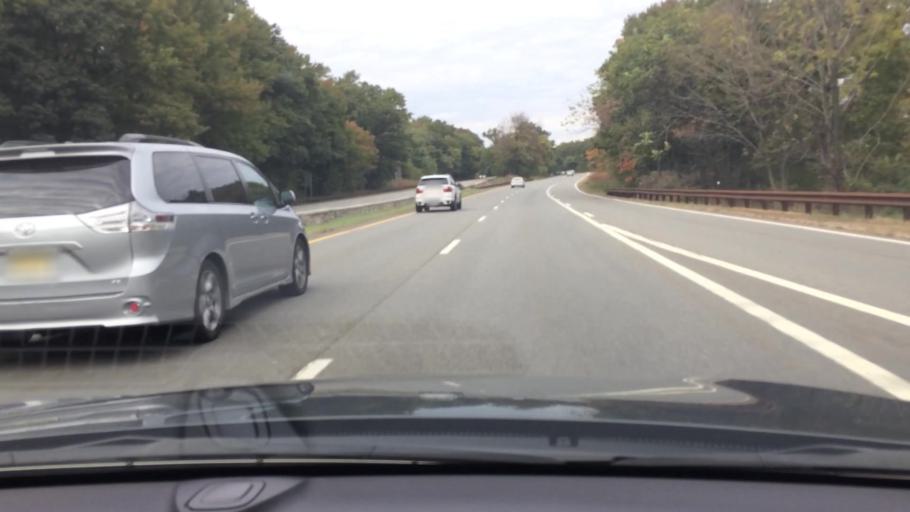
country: US
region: New Jersey
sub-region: Bergen County
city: Englewood Cliffs
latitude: 40.8817
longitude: -73.9475
